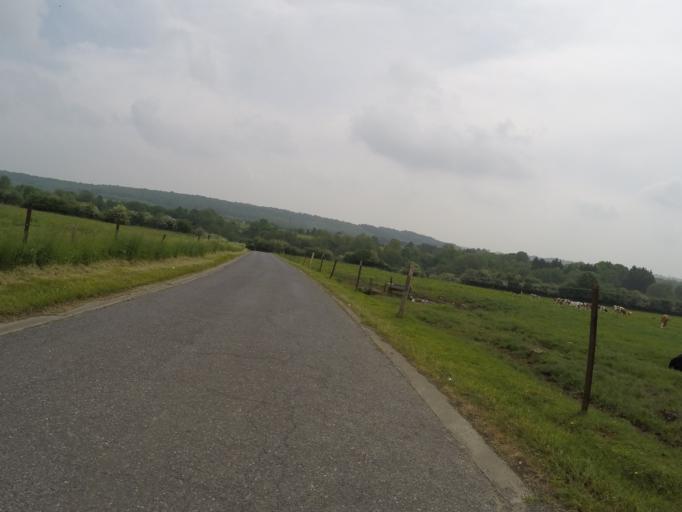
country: BE
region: Wallonia
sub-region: Province de Namur
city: Ciney
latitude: 50.3306
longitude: 5.0655
